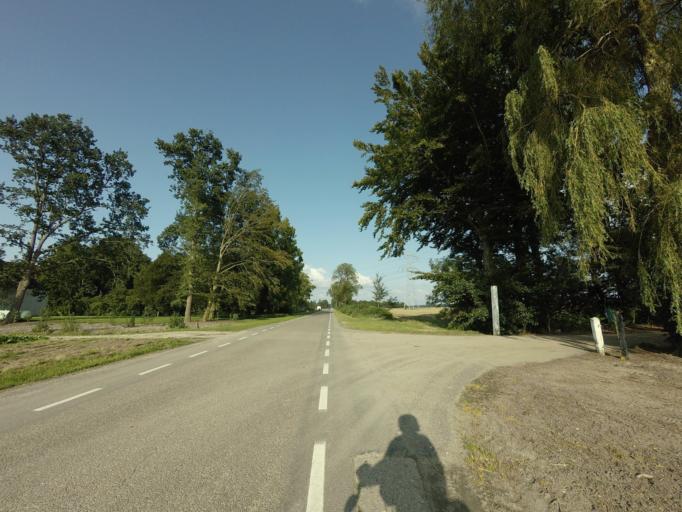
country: NL
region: Flevoland
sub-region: Gemeente Noordoostpolder
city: Ens
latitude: 52.6770
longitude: 5.8160
